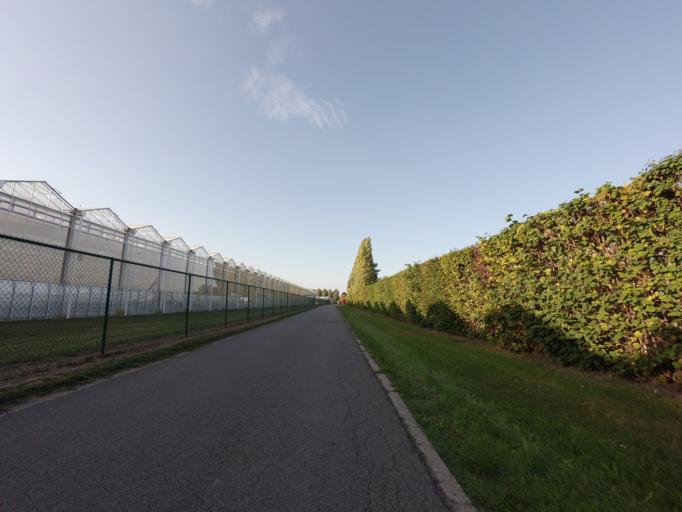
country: BE
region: Flanders
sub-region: Provincie Vlaams-Brabant
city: Haacht
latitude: 50.9393
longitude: 4.6263
